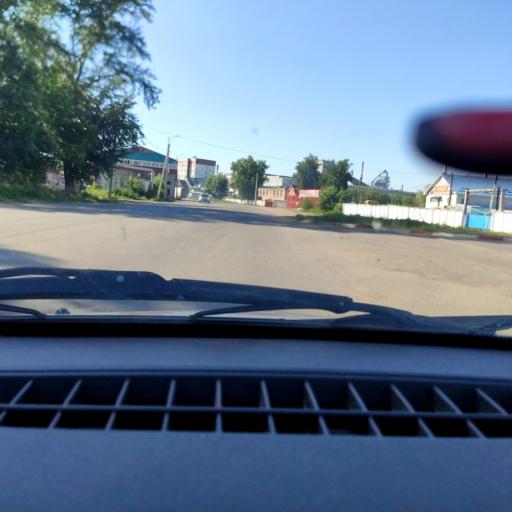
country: RU
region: Bashkortostan
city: Sterlitamak
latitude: 53.6496
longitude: 55.9786
